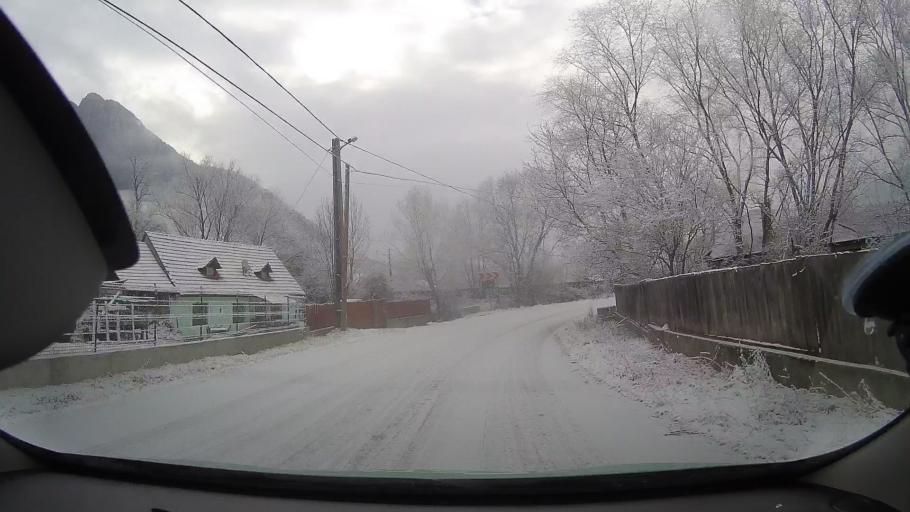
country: RO
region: Alba
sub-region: Comuna Rimetea
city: Rimetea
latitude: 46.4590
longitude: 23.5716
